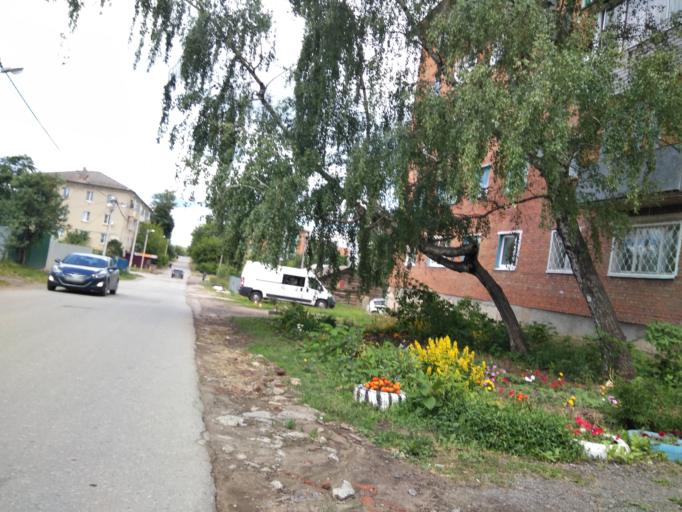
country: RU
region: Tula
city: Lomintsevskiy
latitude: 53.9355
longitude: 37.6302
